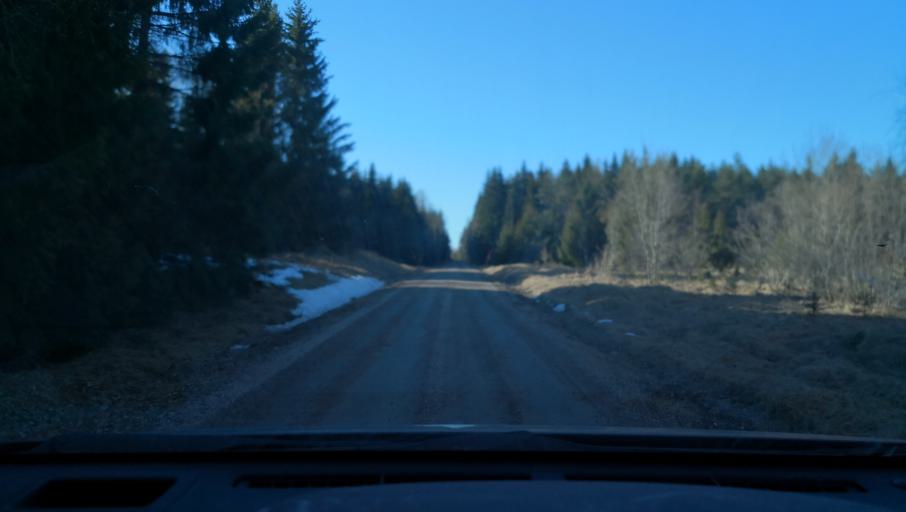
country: SE
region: Vaestmanland
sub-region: Sala Kommun
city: Sala
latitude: 60.1171
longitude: 16.6700
